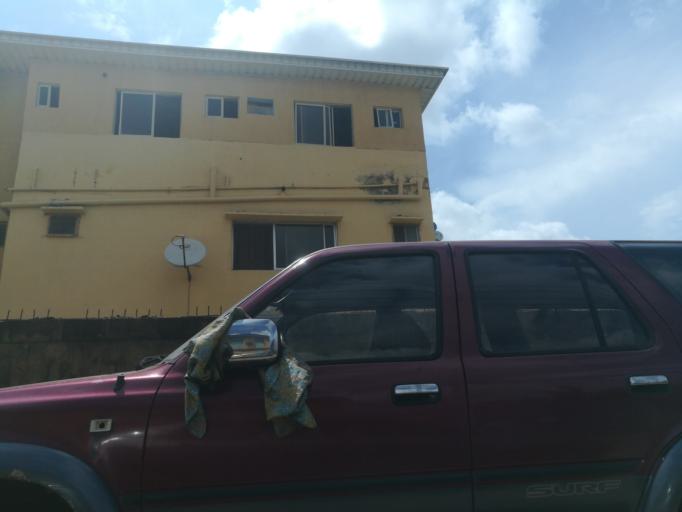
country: NG
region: Lagos
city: Somolu
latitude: 6.5277
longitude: 3.3814
